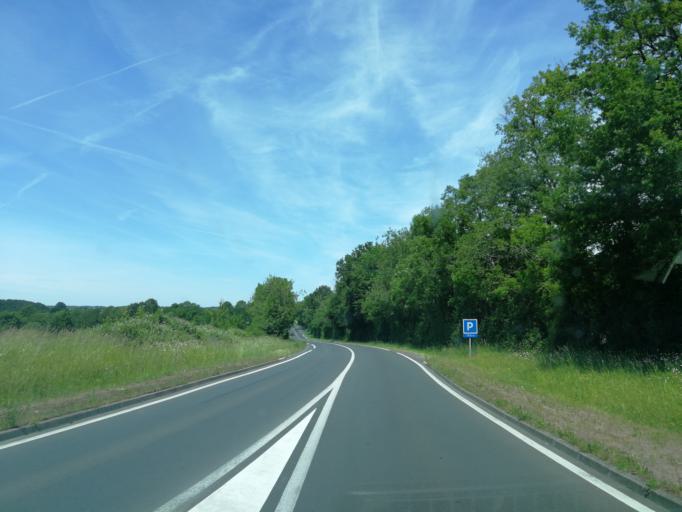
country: FR
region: Pays de la Loire
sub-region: Departement de la Vendee
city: Pissotte
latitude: 46.5164
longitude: -0.8082
